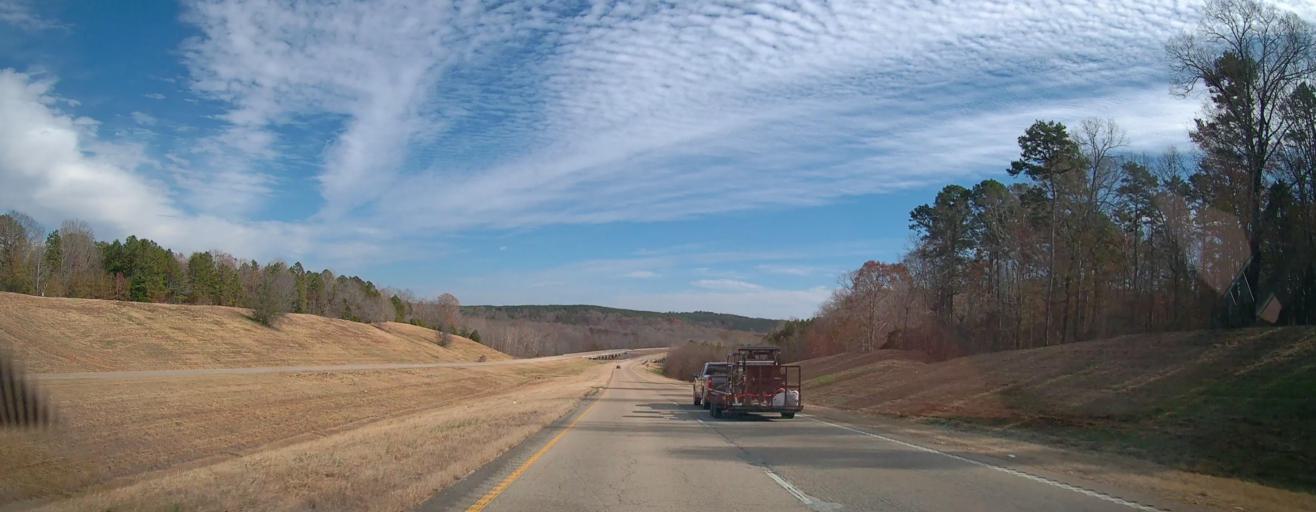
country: US
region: Mississippi
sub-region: Tippah County
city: Ripley
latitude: 34.9459
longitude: -88.7979
